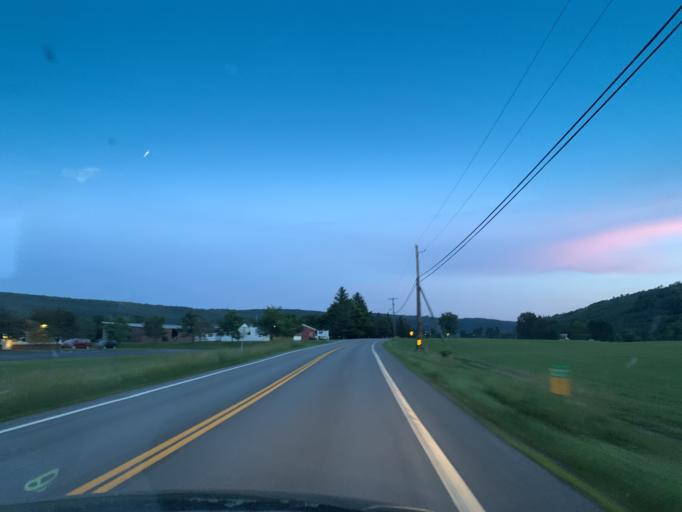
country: US
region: New York
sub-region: Chenango County
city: New Berlin
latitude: 42.5860
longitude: -75.3352
